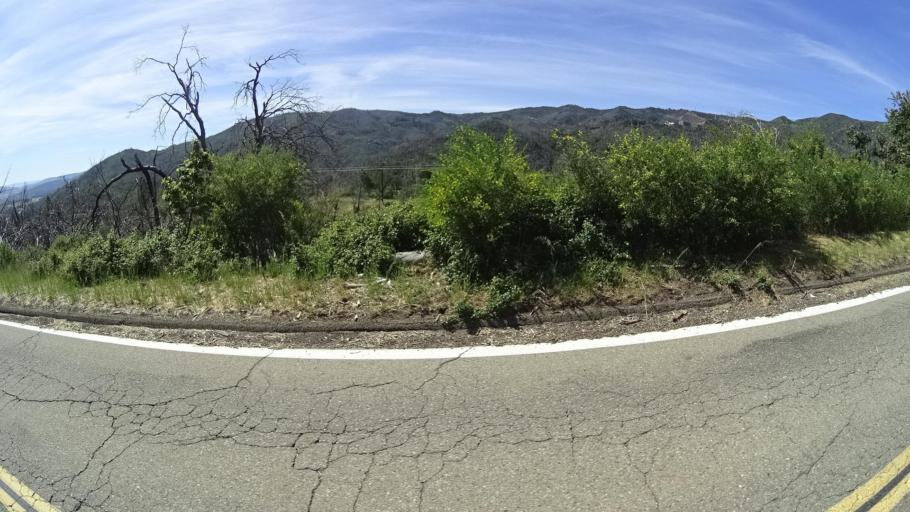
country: US
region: California
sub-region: Lake County
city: Cobb
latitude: 38.7831
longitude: -122.6988
